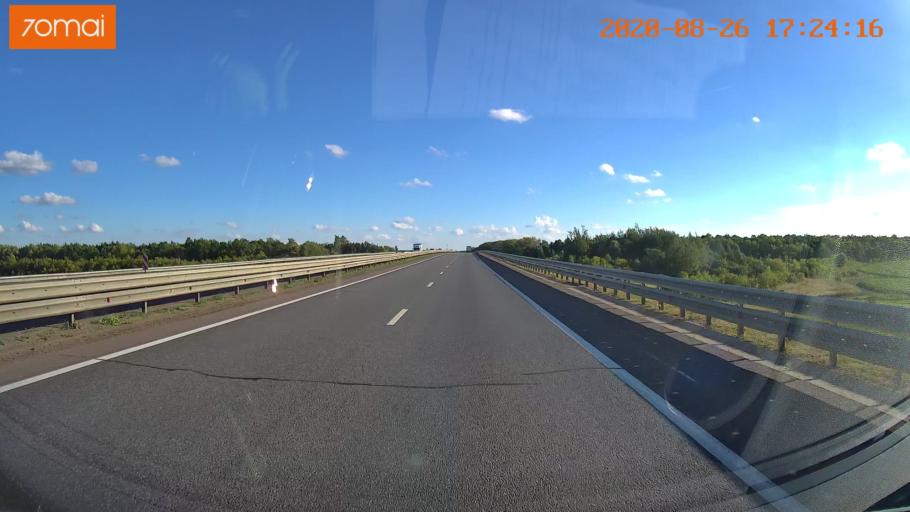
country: RU
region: Tula
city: Volovo
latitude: 53.5205
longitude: 38.1165
